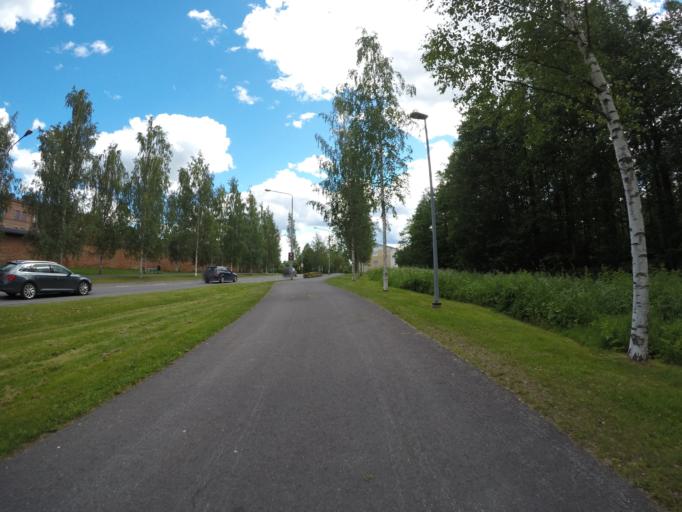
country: FI
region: Haeme
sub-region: Haemeenlinna
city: Haemeenlinna
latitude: 61.0044
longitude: 24.4542
